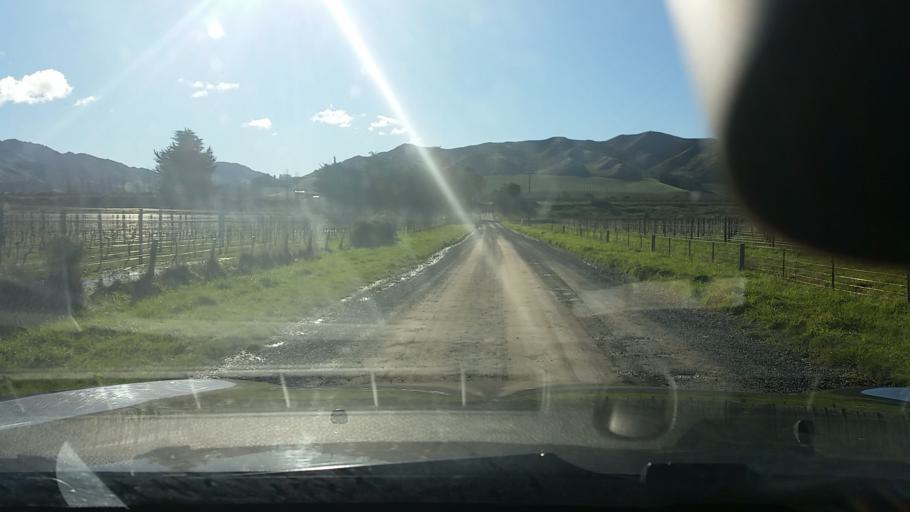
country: NZ
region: Marlborough
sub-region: Marlborough District
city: Blenheim
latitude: -41.6495
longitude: 174.0551
